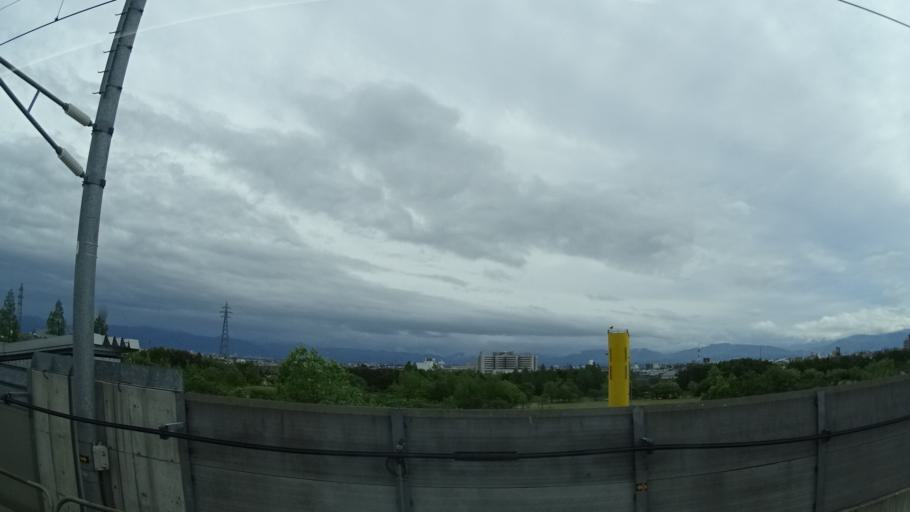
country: JP
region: Toyama
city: Toyama-shi
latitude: 36.6999
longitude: 137.2313
